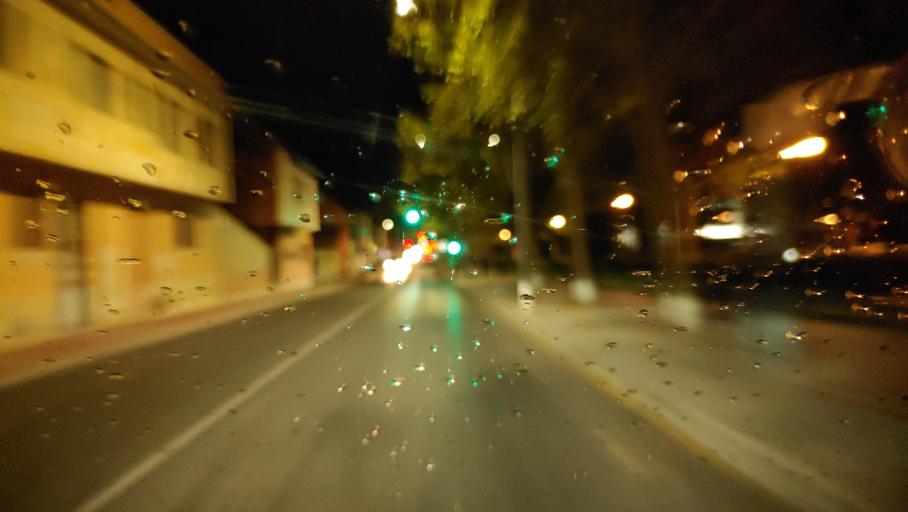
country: ES
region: Castille-La Mancha
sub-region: Provincia de Ciudad Real
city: Ciudad Real
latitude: 38.9766
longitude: -3.9278
